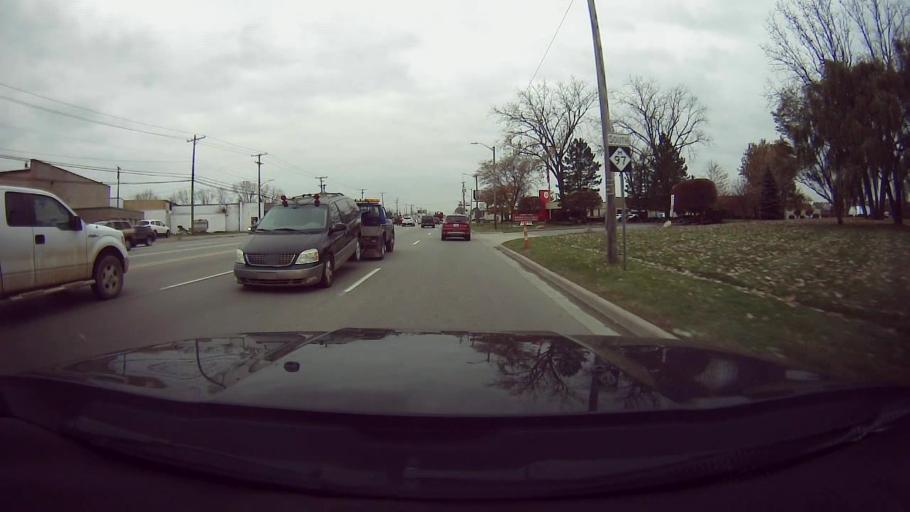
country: US
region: Michigan
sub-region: Macomb County
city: Roseville
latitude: 42.5024
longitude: -82.9630
